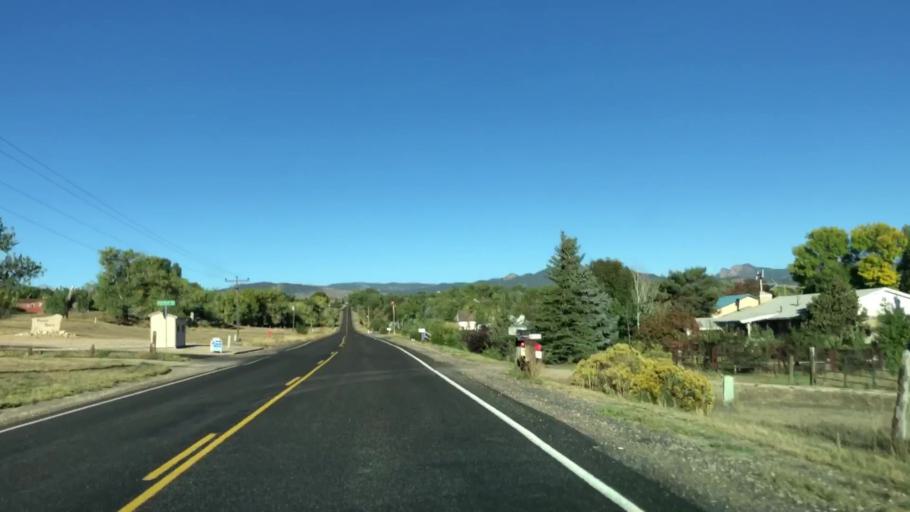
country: US
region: Colorado
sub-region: Larimer County
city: Loveland
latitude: 40.3786
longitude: -105.1440
